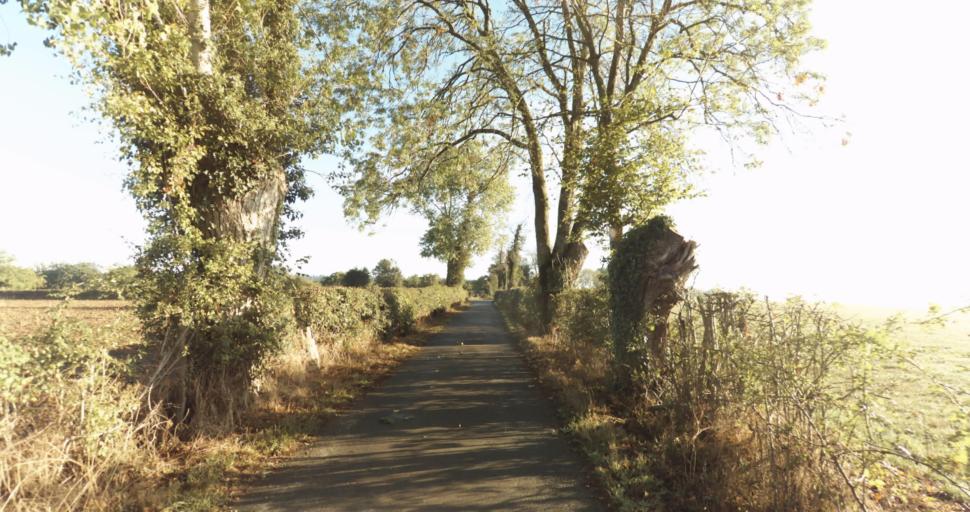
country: FR
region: Lower Normandy
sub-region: Departement de l'Orne
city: Vimoutiers
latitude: 48.9177
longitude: 0.1557
